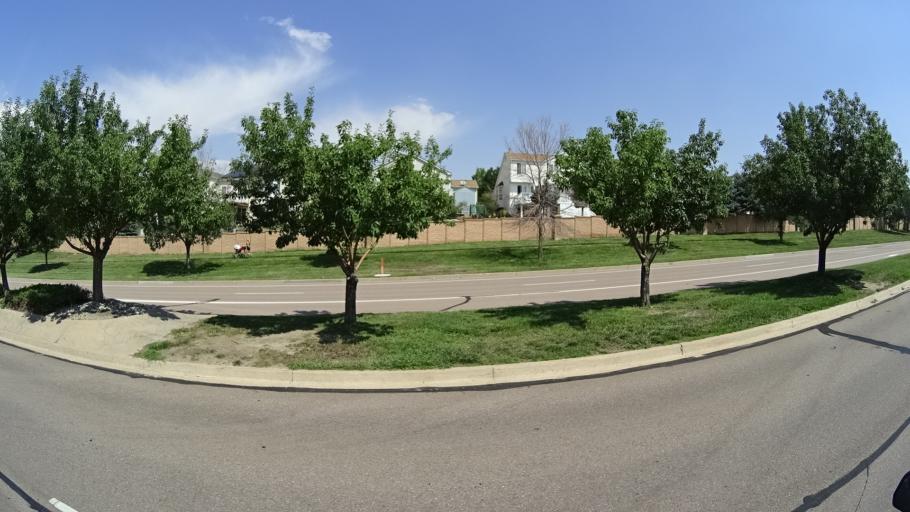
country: US
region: Colorado
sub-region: El Paso County
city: Cimarron Hills
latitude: 38.9292
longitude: -104.7308
